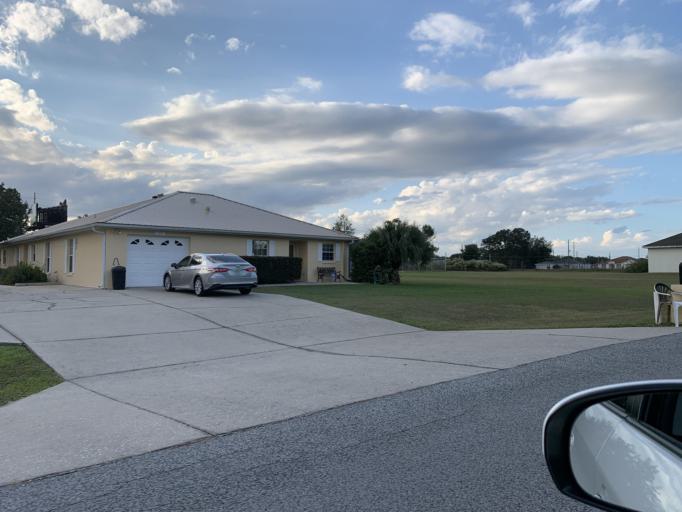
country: US
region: Florida
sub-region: Marion County
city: Silver Springs Shores
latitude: 29.1647
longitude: -82.0518
